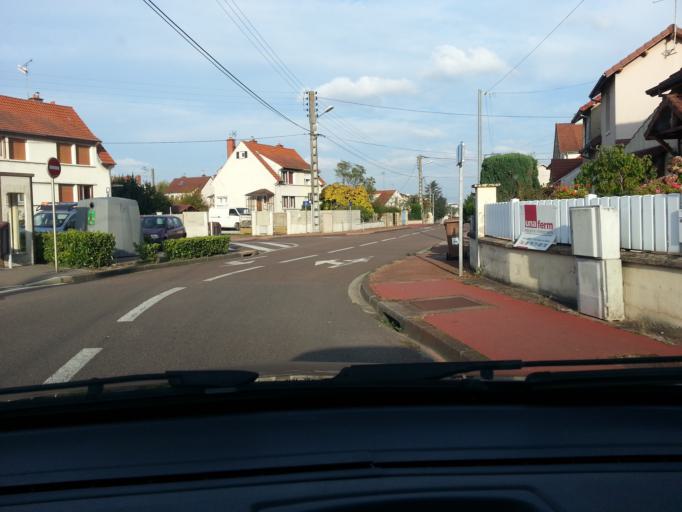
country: FR
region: Bourgogne
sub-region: Departement de Saone-et-Loire
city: Chatenoy-le-Royal
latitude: 46.7794
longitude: 4.8222
